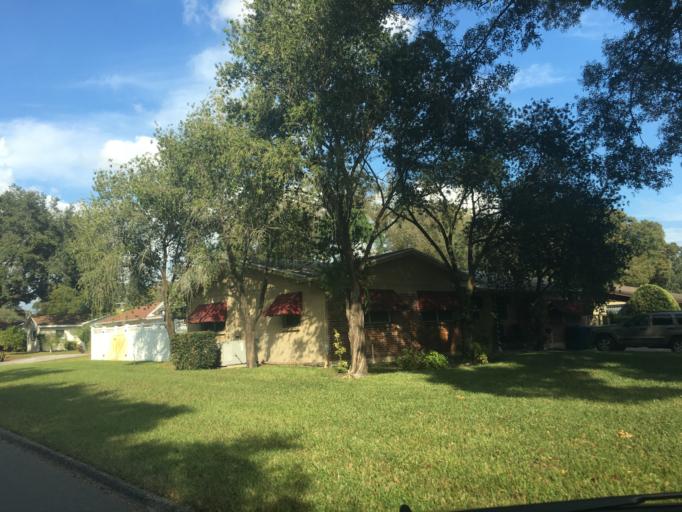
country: US
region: Florida
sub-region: Hillsborough County
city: Tampa
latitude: 27.9893
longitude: -82.4722
